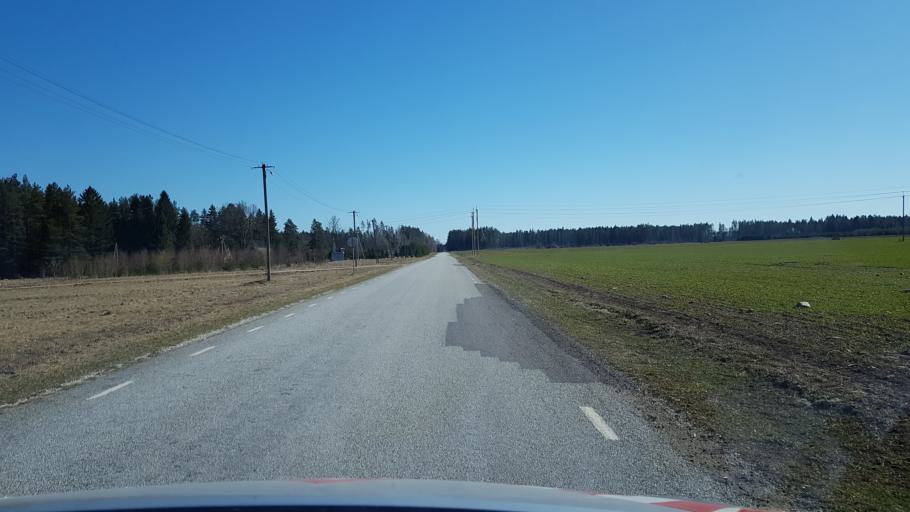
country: EE
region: Laeaene-Virumaa
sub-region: Viru-Nigula vald
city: Kunda
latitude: 59.3903
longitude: 26.5699
